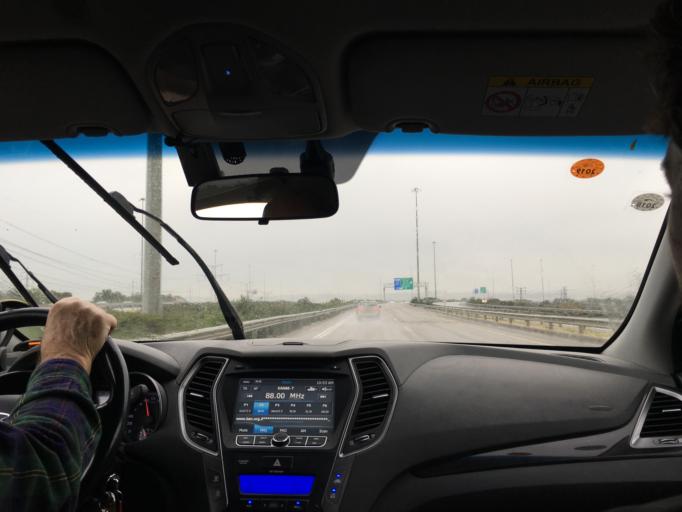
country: IL
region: Central District
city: Rosh Ha'Ayin
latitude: 32.1160
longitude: 34.9308
